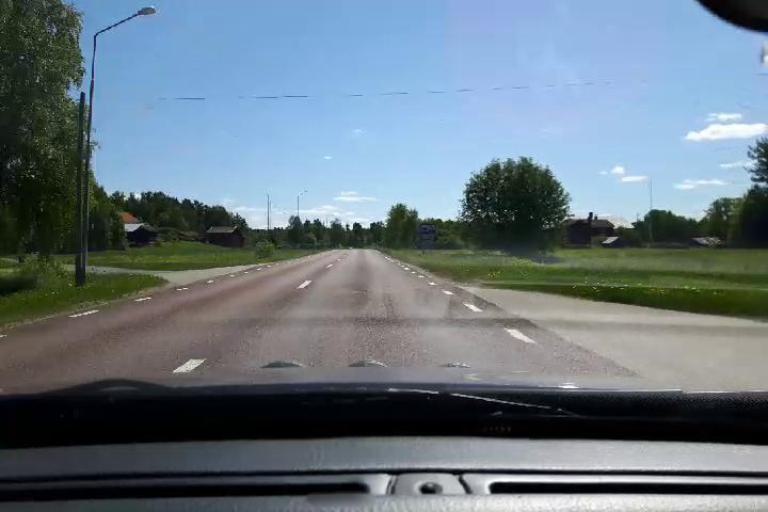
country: SE
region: Jaemtland
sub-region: Harjedalens Kommun
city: Sveg
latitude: 62.1594
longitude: 14.9516
